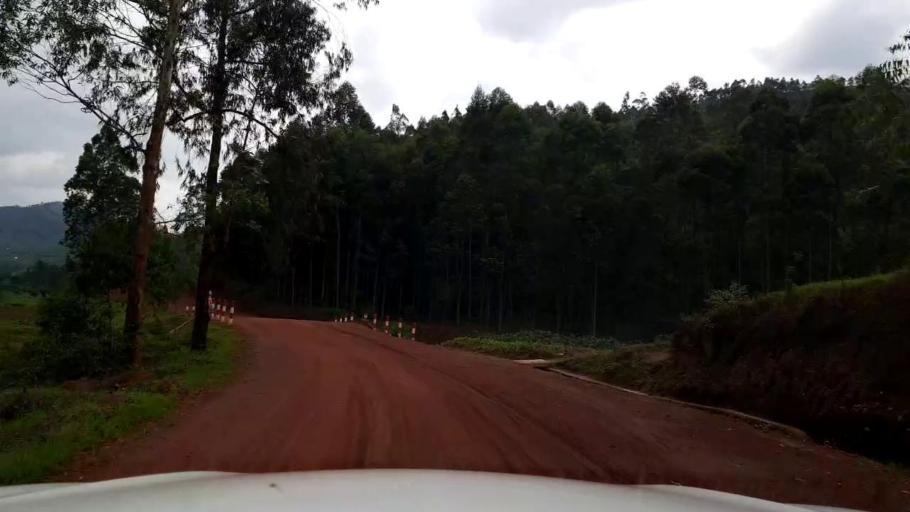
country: RW
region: Northern Province
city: Musanze
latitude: -1.6731
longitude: 29.7988
